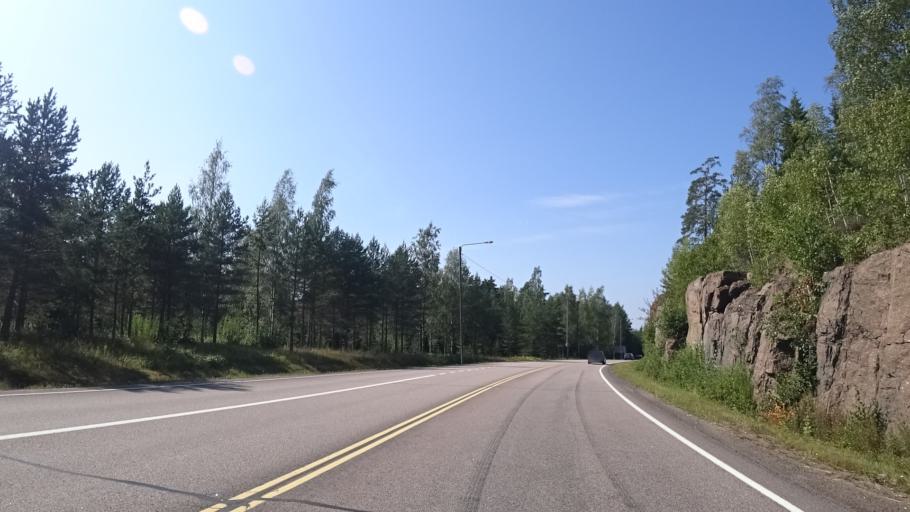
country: FI
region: Kymenlaakso
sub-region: Kotka-Hamina
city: Hamina
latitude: 60.5656
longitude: 27.1183
